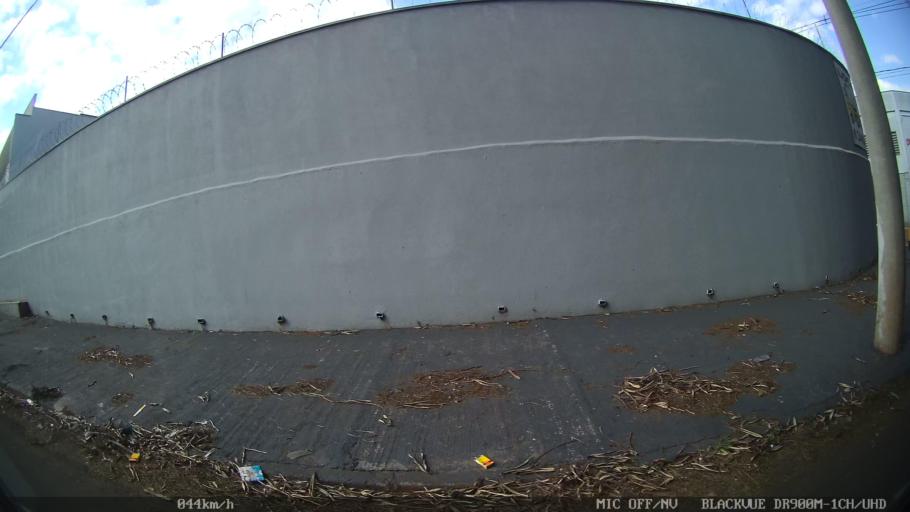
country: BR
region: Sao Paulo
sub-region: Americana
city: Americana
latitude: -22.7251
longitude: -47.3279
